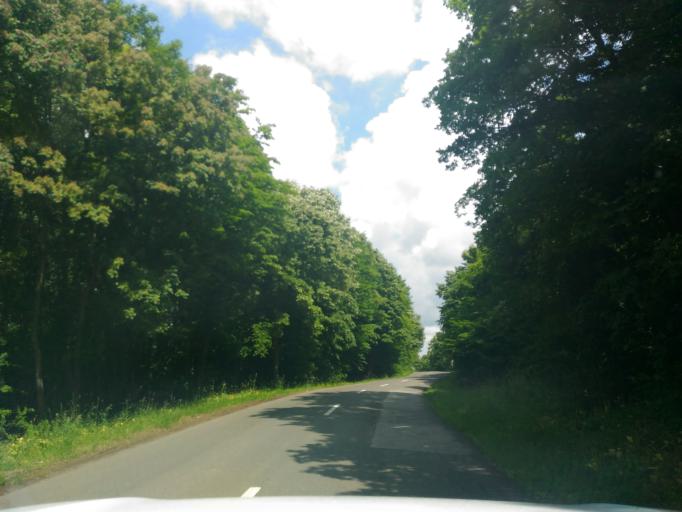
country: HU
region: Baranya
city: Pecs
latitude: 46.1140
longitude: 18.1980
